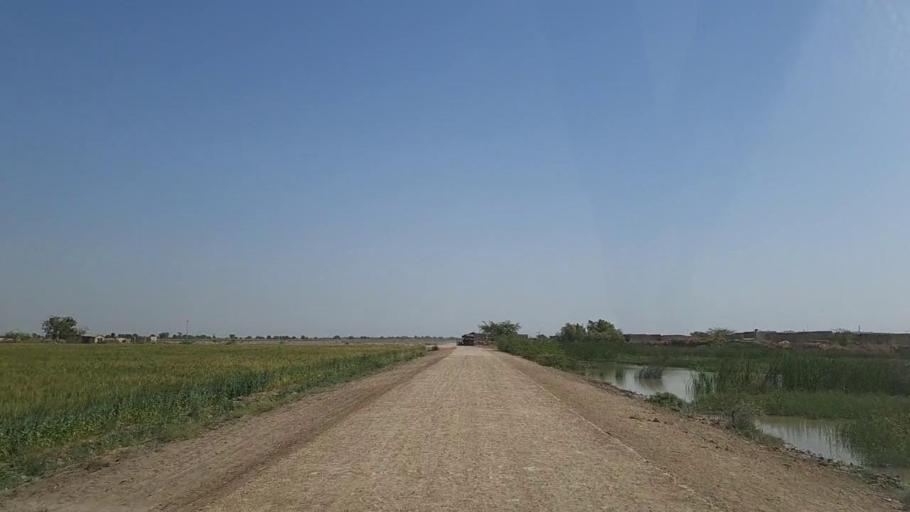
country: PK
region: Sindh
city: Samaro
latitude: 25.1742
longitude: 69.4024
